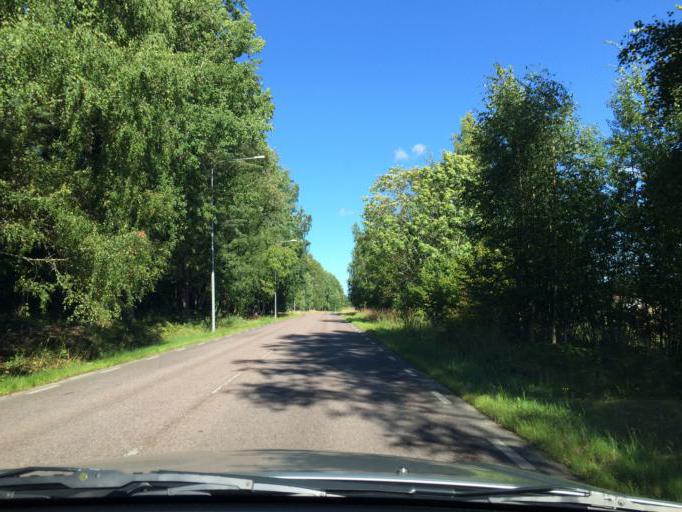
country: SE
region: Vaestmanland
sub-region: Vasteras
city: Vasteras
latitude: 59.5848
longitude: 16.6177
